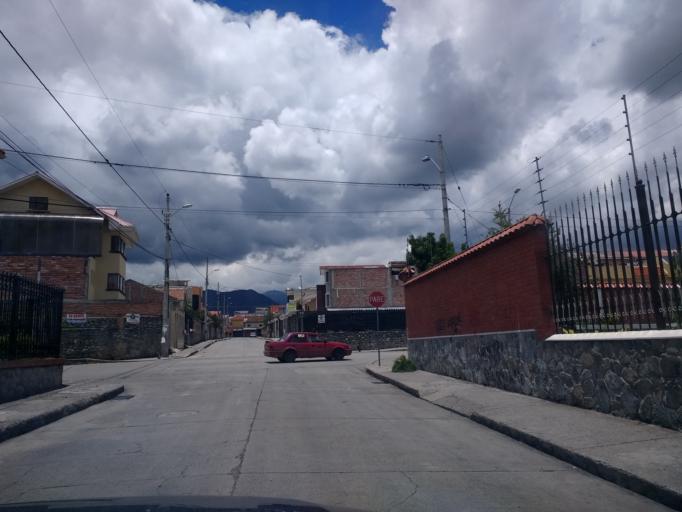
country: EC
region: Azuay
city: Cuenca
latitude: -2.9004
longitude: -79.0332
